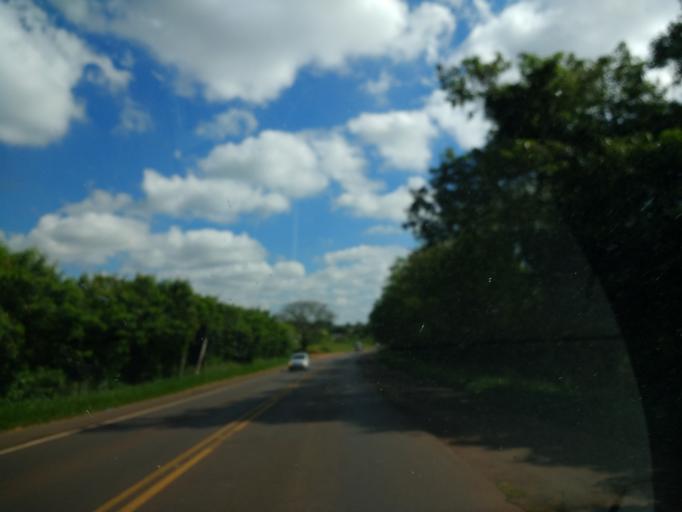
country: BR
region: Parana
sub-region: Alto Piquiri
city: Alto Piquiri
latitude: -23.8907
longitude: -53.4108
